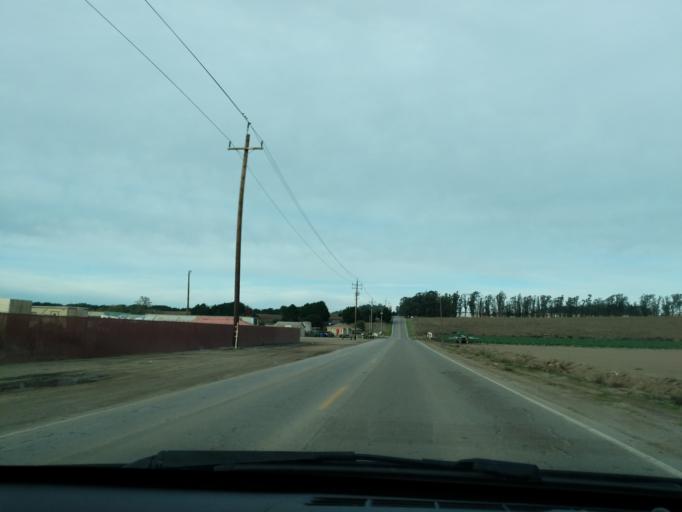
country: US
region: California
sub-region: Santa Barbara County
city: Guadalupe
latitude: 35.0158
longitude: -120.5655
